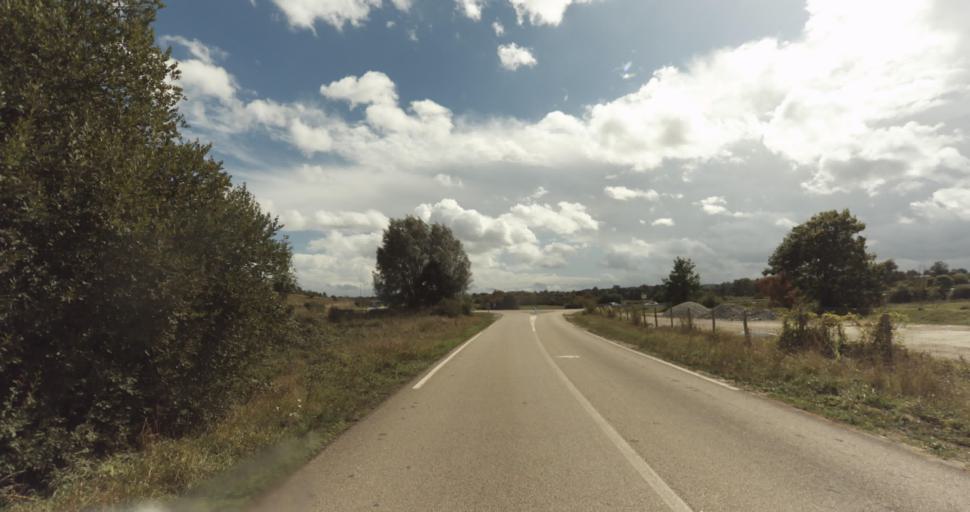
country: FR
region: Lower Normandy
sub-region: Departement de l'Orne
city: Gace
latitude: 48.7794
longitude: 0.3014
